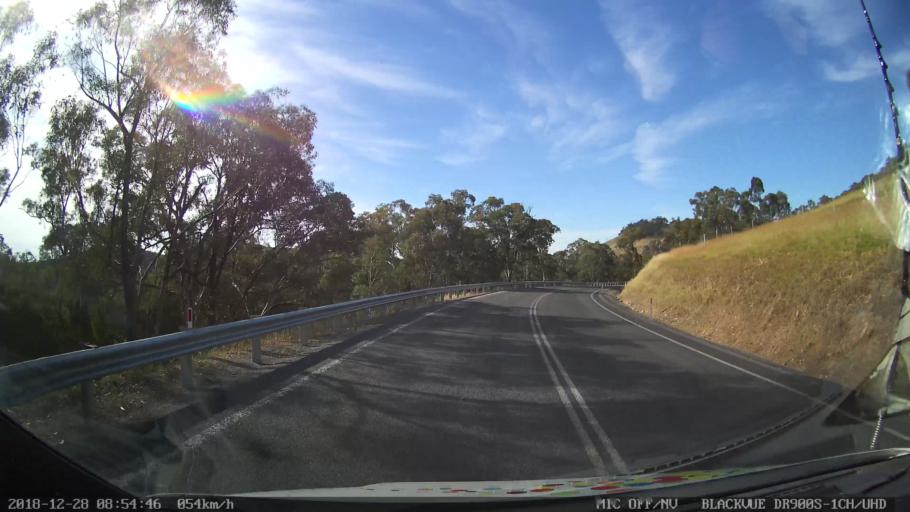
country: AU
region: New South Wales
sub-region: Upper Lachlan Shire
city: Crookwell
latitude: -34.0948
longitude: 149.3327
